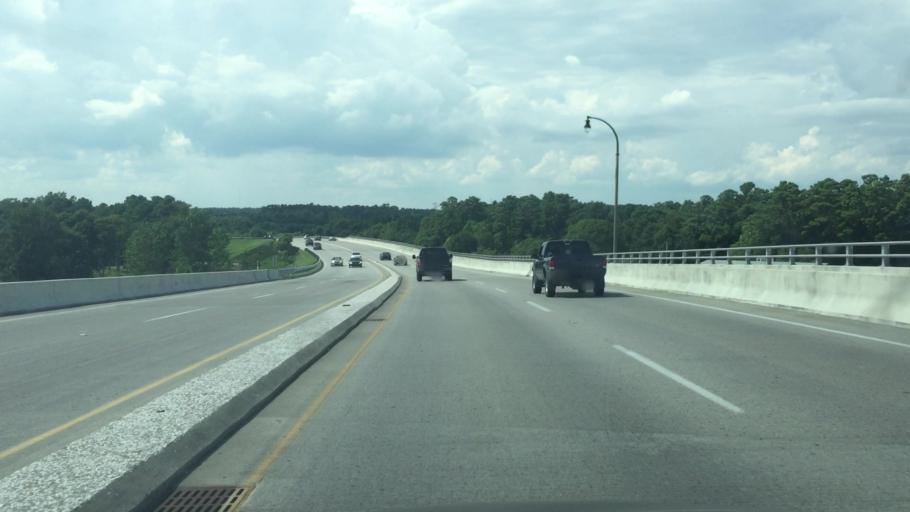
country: US
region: South Carolina
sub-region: Horry County
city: North Myrtle Beach
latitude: 33.8346
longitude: -78.6848
